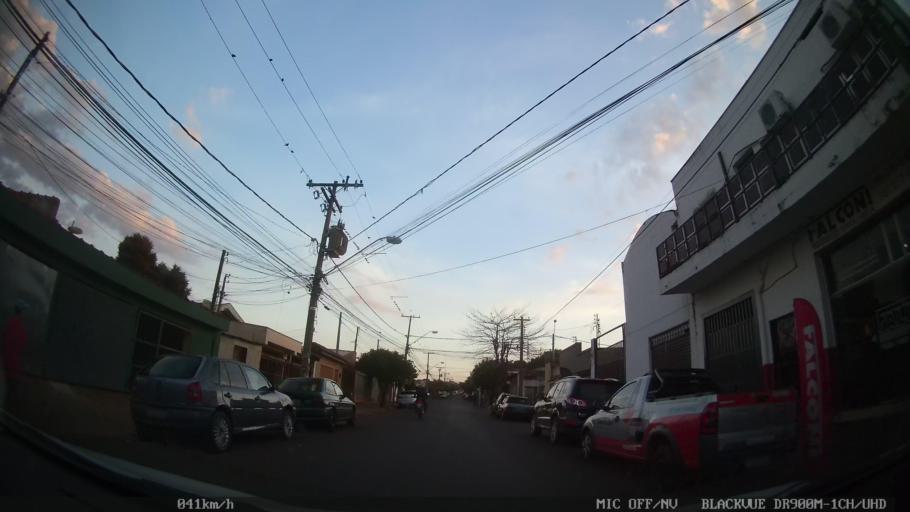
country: BR
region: Sao Paulo
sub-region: Ribeirao Preto
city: Ribeirao Preto
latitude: -21.1478
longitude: -47.8240
